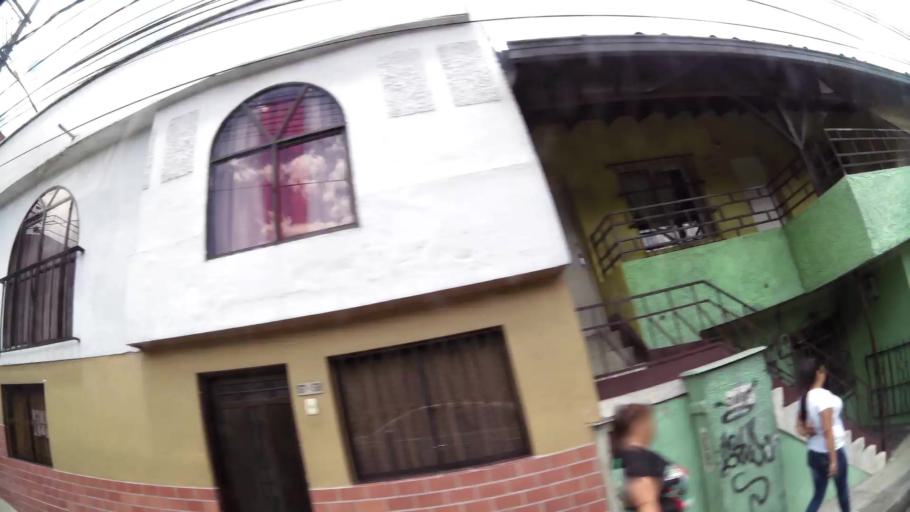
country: CO
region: Antioquia
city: La Estrella
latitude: 6.1571
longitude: -75.6408
